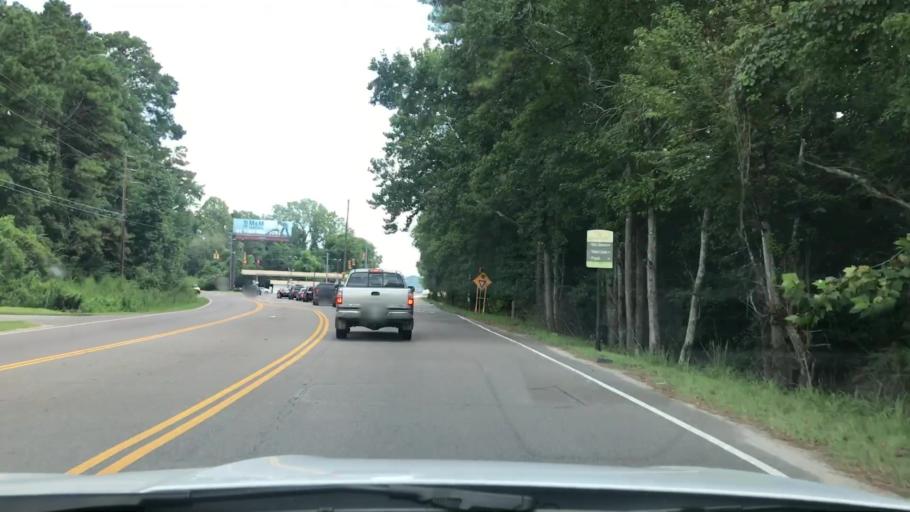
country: US
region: South Carolina
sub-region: Dorchester County
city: Summerville
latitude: 33.0342
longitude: -80.2001
